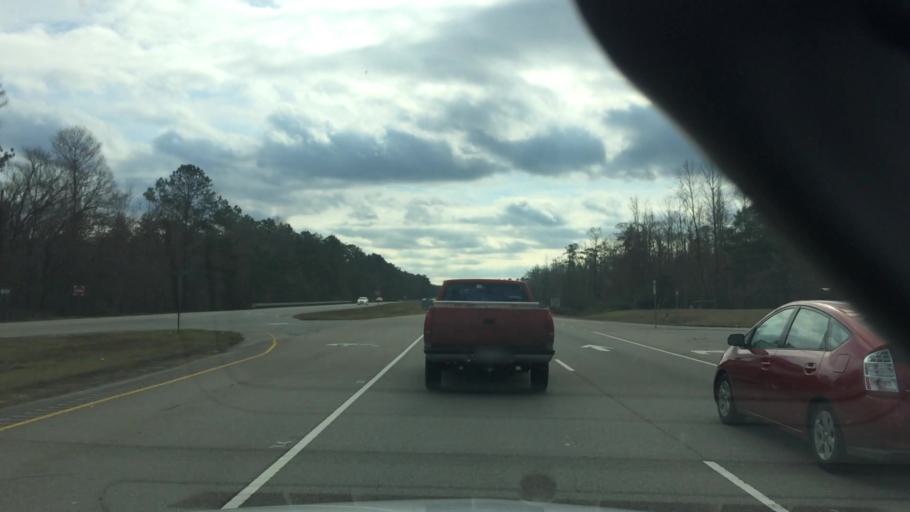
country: US
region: North Carolina
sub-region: Brunswick County
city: Leland
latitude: 34.1603
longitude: -78.0911
